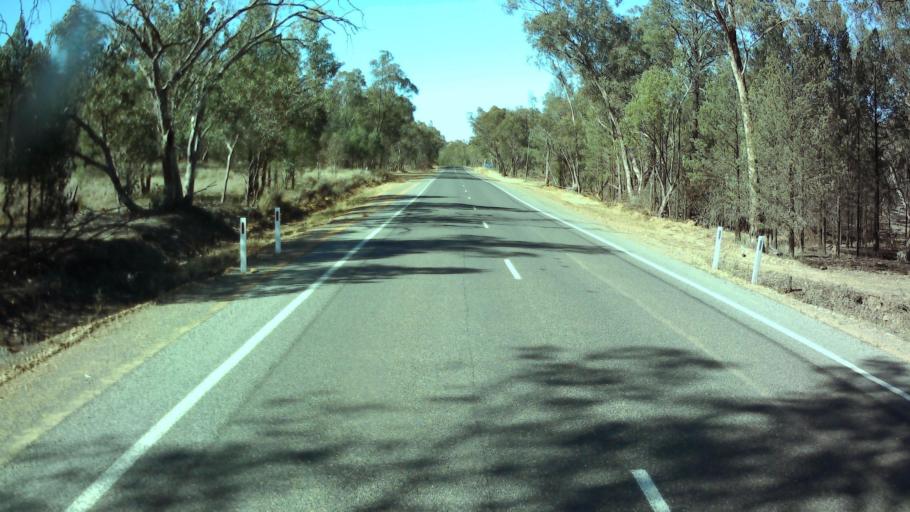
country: AU
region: New South Wales
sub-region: Weddin
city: Grenfell
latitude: -33.7490
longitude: 148.0861
